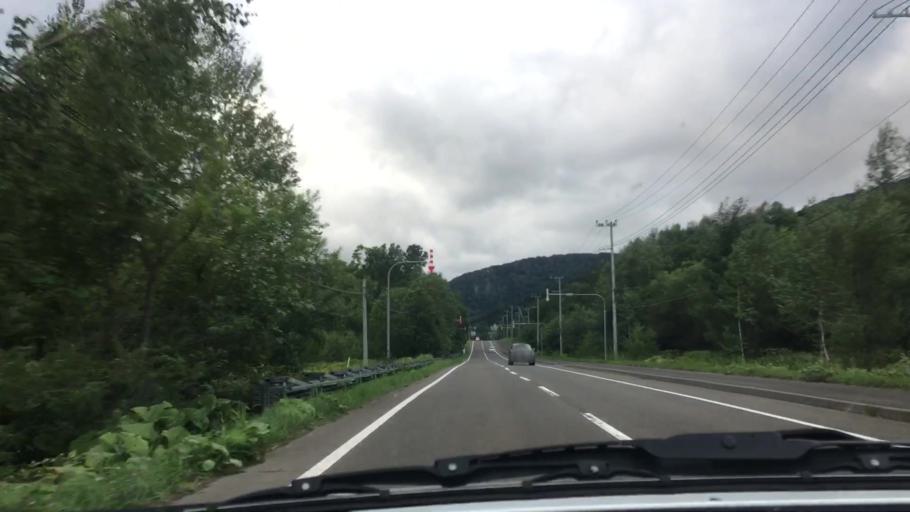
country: JP
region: Hokkaido
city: Shimo-furano
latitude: 43.0559
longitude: 142.6230
